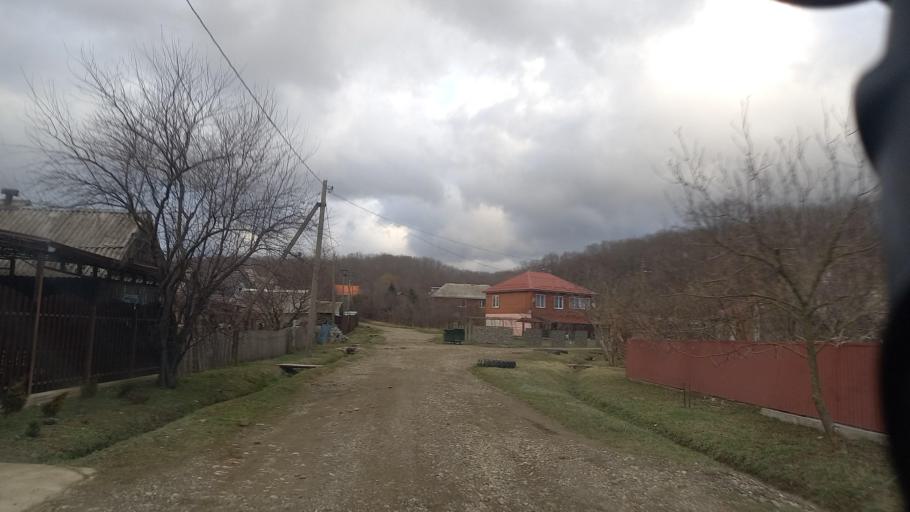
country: RU
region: Krasnodarskiy
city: Lermontovo
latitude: 44.4325
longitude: 38.7945
